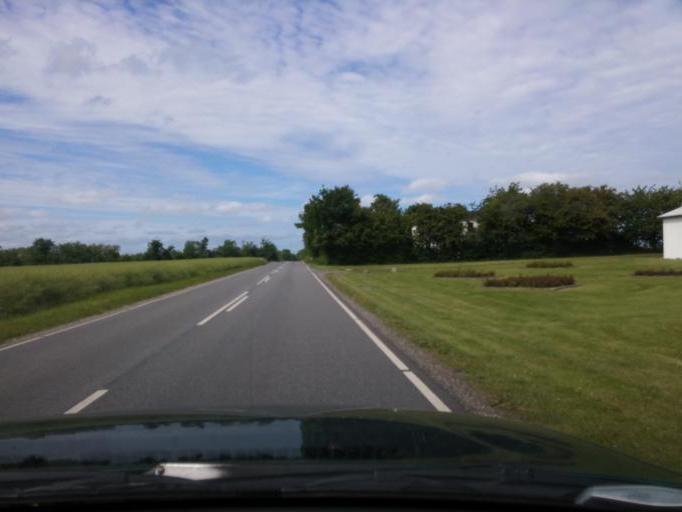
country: DK
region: South Denmark
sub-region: Kerteminde Kommune
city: Langeskov
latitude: 55.4004
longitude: 10.5554
